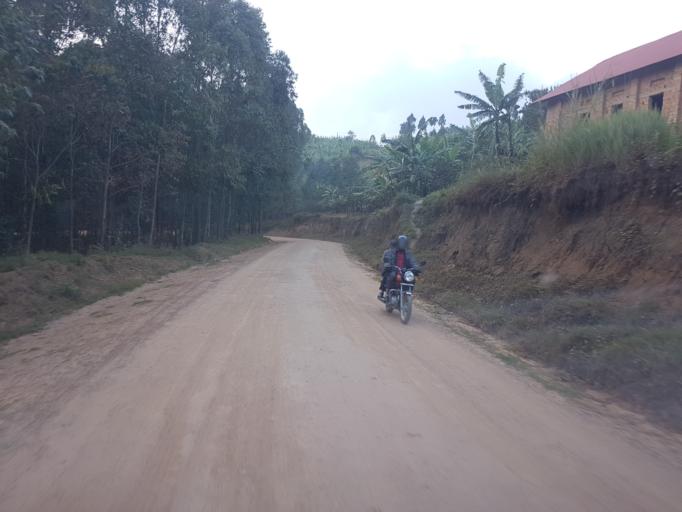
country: UG
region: Western Region
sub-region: Rukungiri District
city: Rukungiri
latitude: -0.7286
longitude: 29.9469
